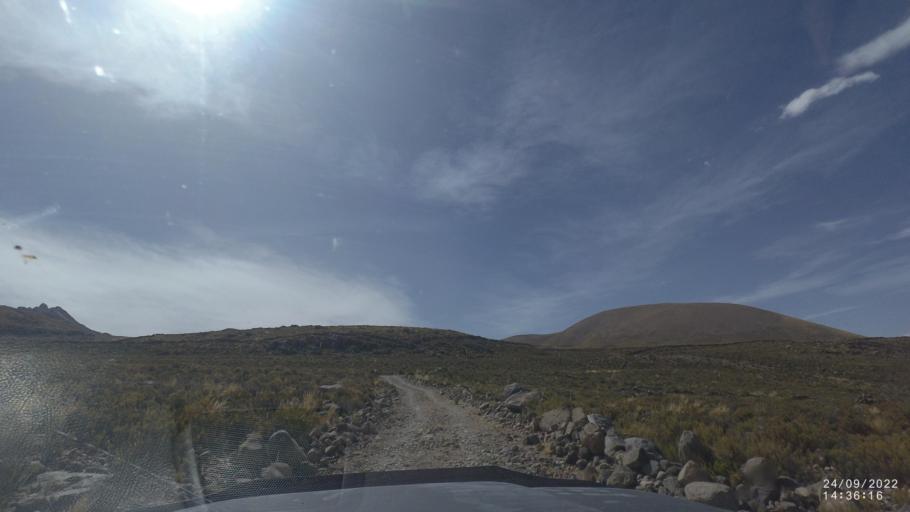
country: BO
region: Potosi
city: Colchani
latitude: -19.8542
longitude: -67.5794
